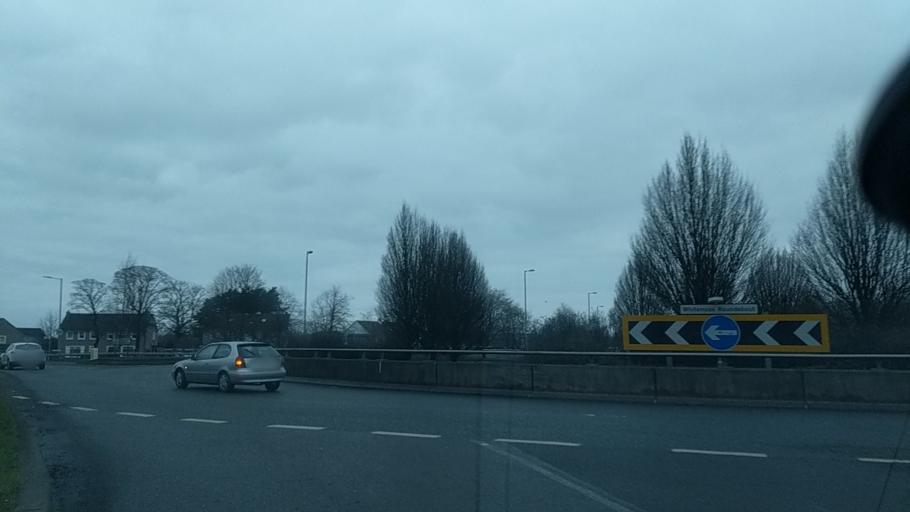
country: GB
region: Scotland
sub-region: South Lanarkshire
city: East Kilbride
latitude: 55.7628
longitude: -4.1655
